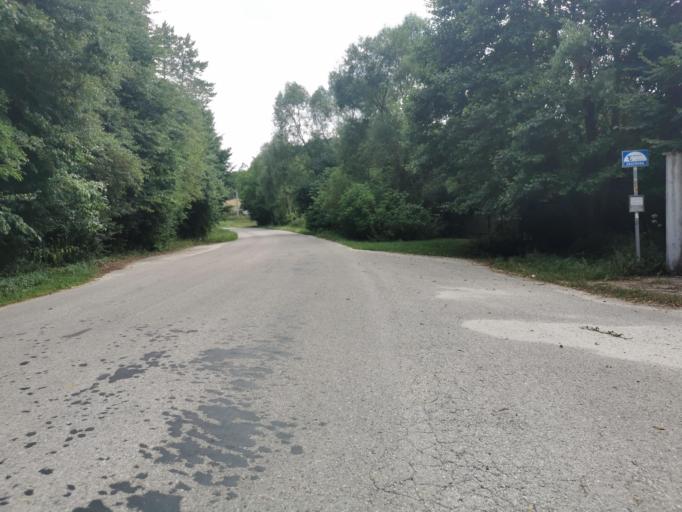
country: SK
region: Trenciansky
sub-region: Okres Myjava
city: Myjava
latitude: 48.7392
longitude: 17.5129
